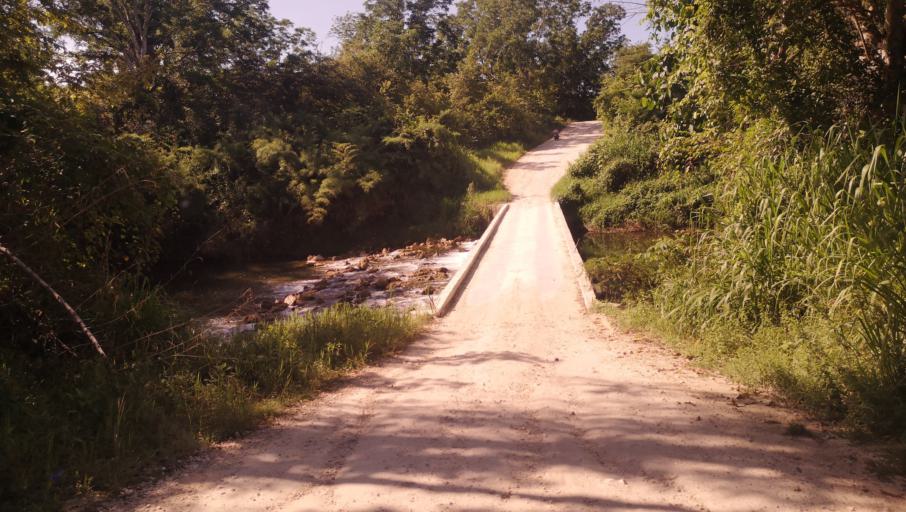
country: GT
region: Peten
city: Dolores
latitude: 16.7239
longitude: -89.3572
